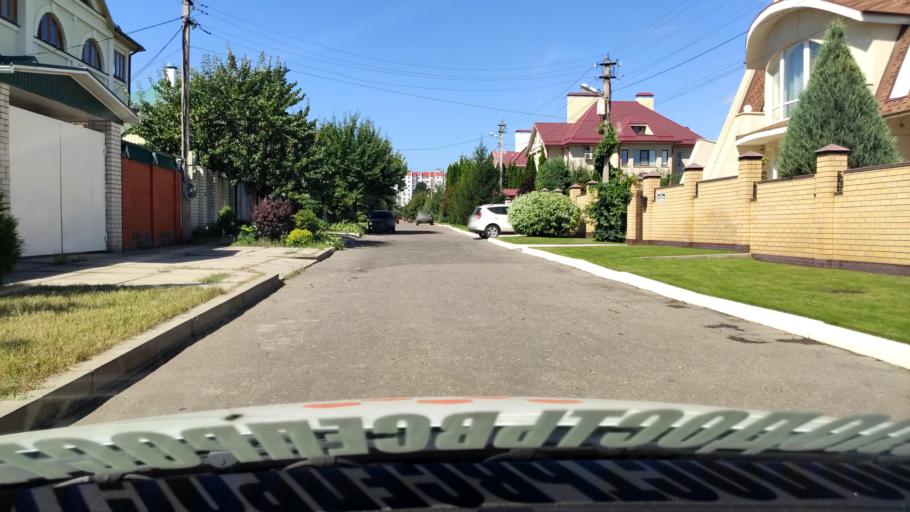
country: RU
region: Voronezj
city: Voronezh
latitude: 51.7048
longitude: 39.2021
